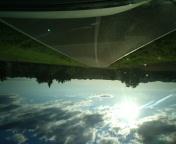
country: DE
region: Baden-Wuerttemberg
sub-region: Karlsruhe Region
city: Dobel
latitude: 48.8634
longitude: 8.5238
